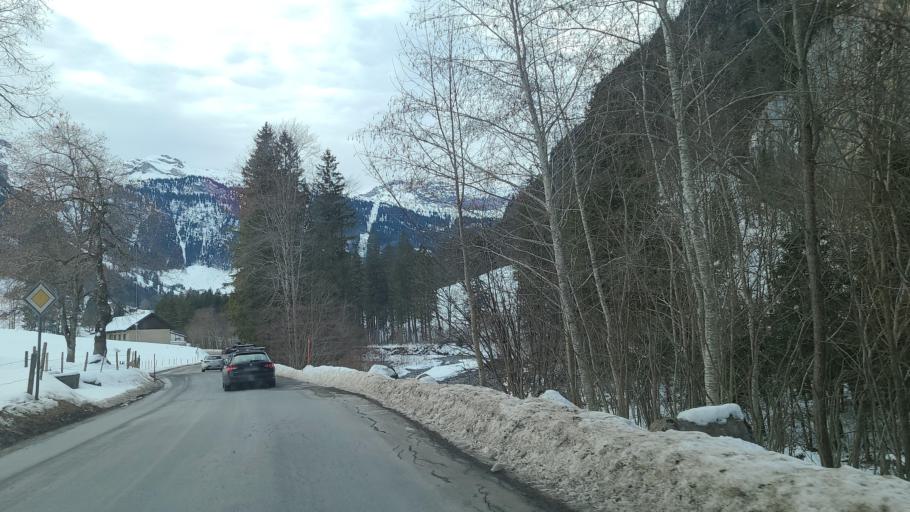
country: CH
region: Obwalden
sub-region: Obwalden
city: Sachseln
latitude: 46.8204
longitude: 8.2837
